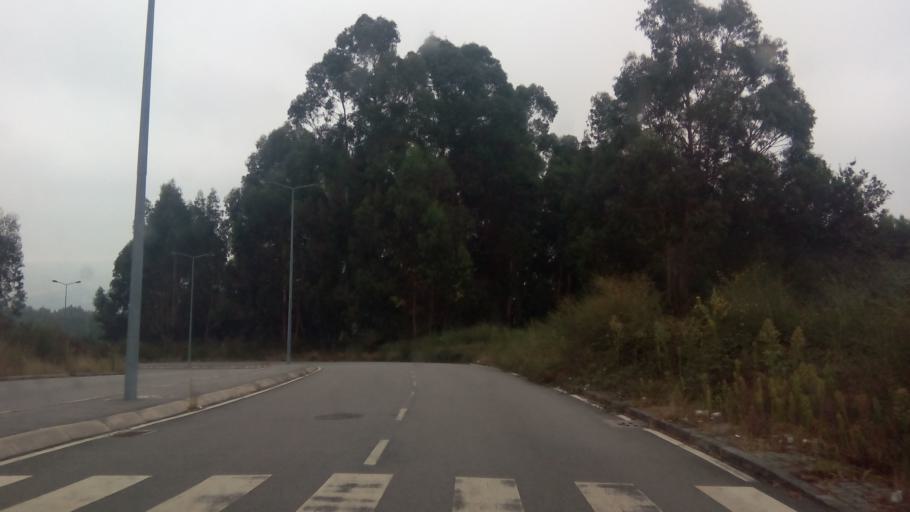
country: PT
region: Porto
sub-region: Paredes
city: Madalena
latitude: 41.2206
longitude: -8.3682
